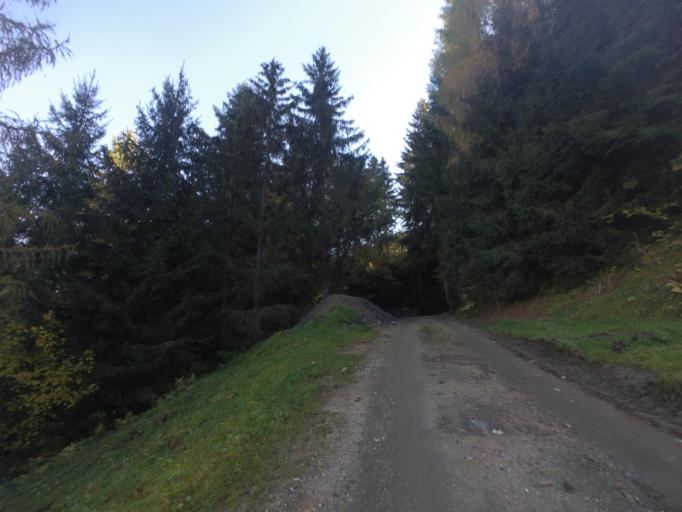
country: AT
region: Salzburg
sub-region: Politischer Bezirk Sankt Johann im Pongau
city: Sankt Johann im Pongau
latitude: 47.3294
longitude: 13.2179
